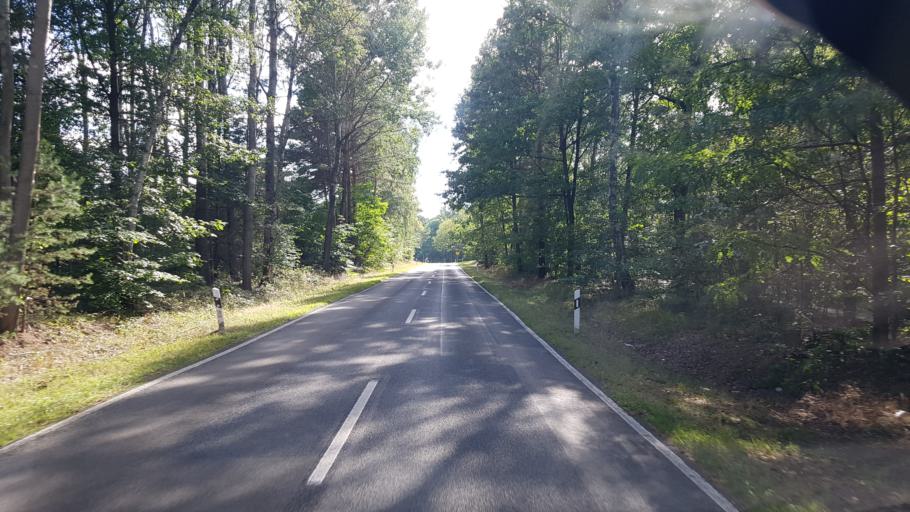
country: DE
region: Brandenburg
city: Tschernitz
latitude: 51.6055
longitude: 14.5850
